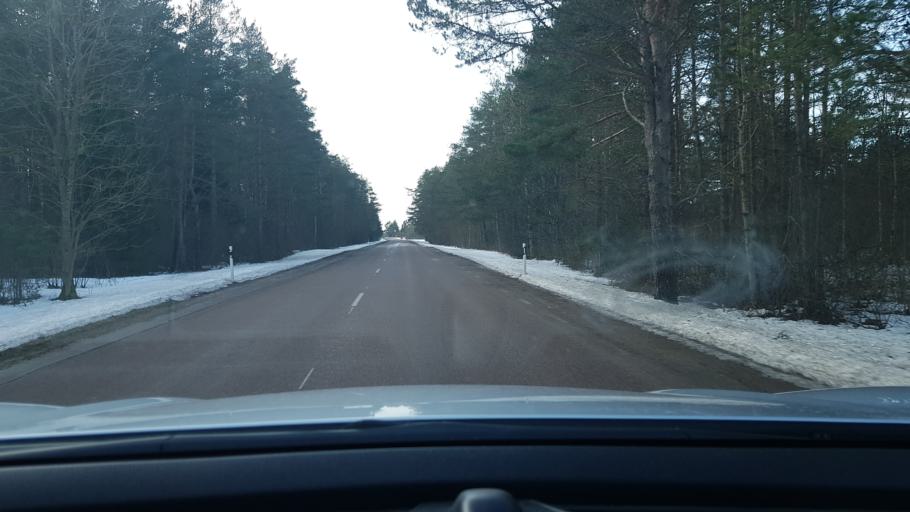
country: EE
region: Saare
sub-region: Kuressaare linn
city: Kuressaare
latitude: 58.3423
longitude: 22.5792
